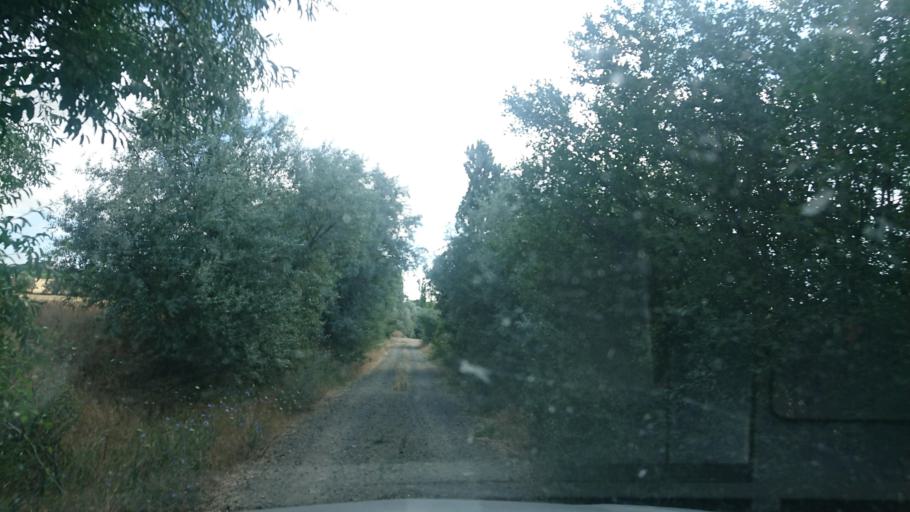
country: TR
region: Aksaray
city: Agacoren
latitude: 38.8611
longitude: 33.9405
